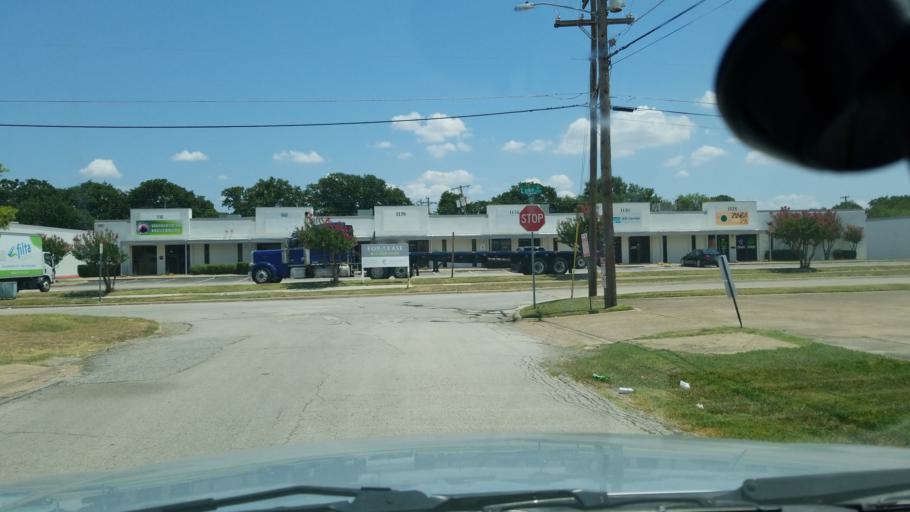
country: US
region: Texas
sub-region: Dallas County
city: Irving
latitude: 32.8261
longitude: -96.9918
